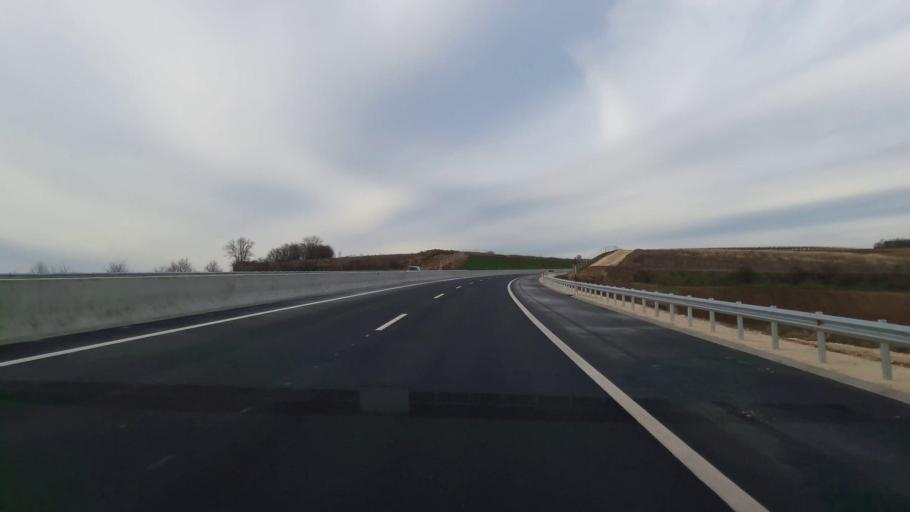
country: AT
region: Lower Austria
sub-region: Politischer Bezirk Mistelbach
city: Herrnbaumgarten
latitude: 48.6843
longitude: 16.6574
